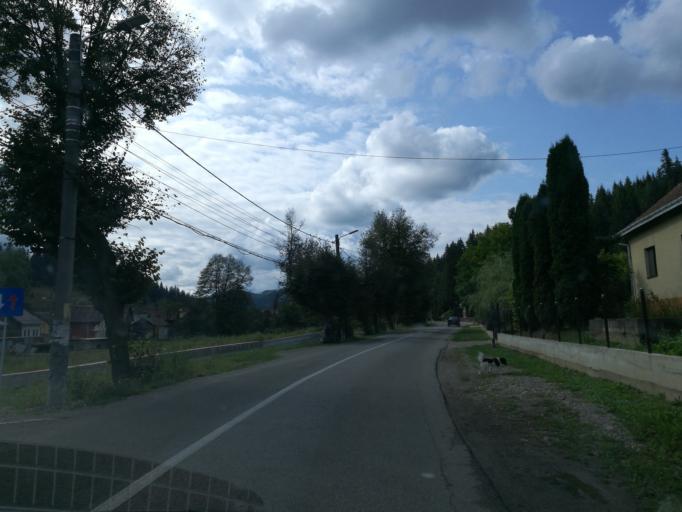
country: RO
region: Suceava
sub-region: Oras Gura Humorului
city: Gura Humorului
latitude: 47.5318
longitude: 25.8643
